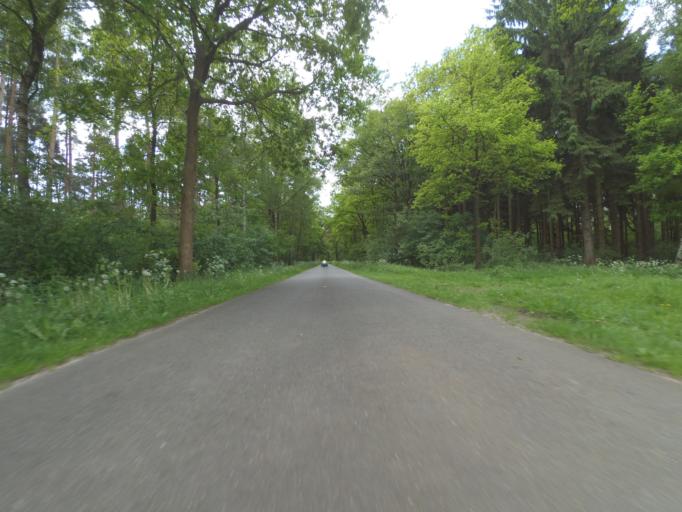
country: DE
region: Lower Saxony
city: Wietze
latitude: 52.5914
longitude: 9.8173
